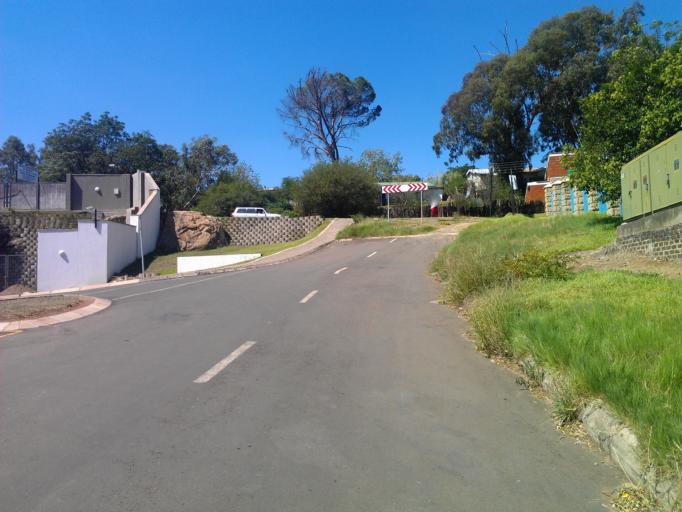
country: LS
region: Maseru
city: Maseru
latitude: -29.3103
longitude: 27.4779
